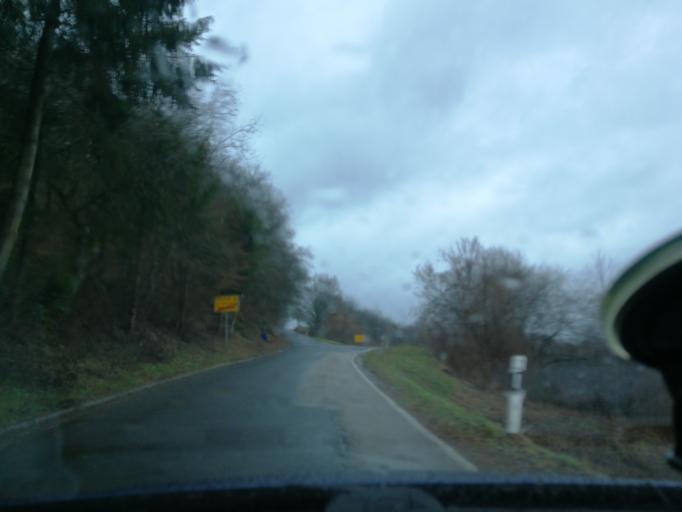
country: DE
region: Rheinland-Pfalz
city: Deuselbach
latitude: 49.7547
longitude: 7.0503
